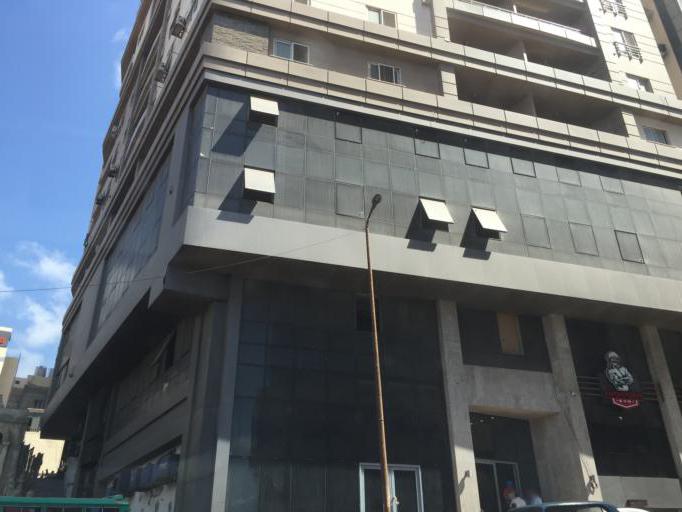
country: EG
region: Alexandria
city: Alexandria
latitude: 31.2618
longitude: 29.9845
